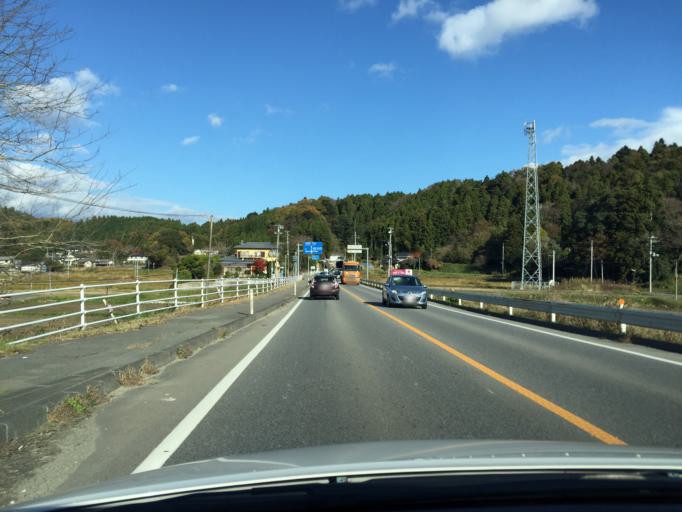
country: JP
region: Fukushima
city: Iwaki
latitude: 37.1751
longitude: 140.9931
